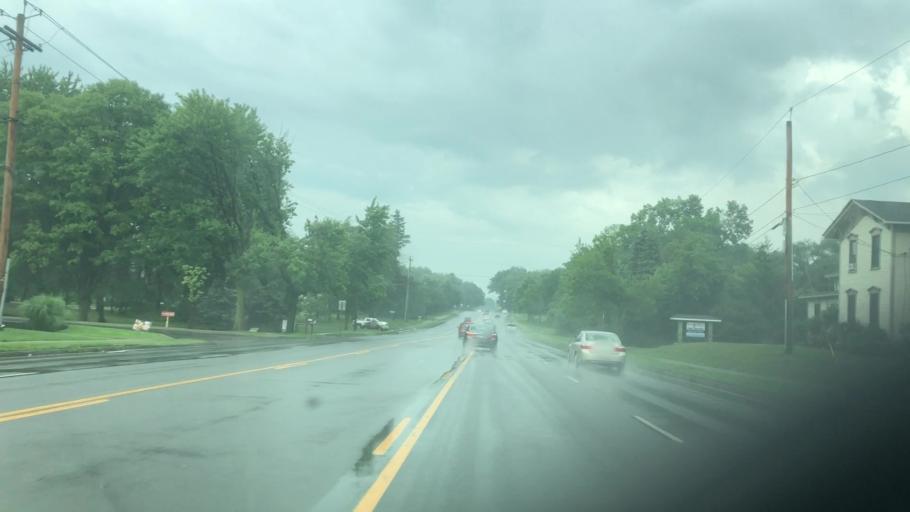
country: US
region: New York
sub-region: Monroe County
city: Fairport
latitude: 43.1307
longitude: -77.4371
